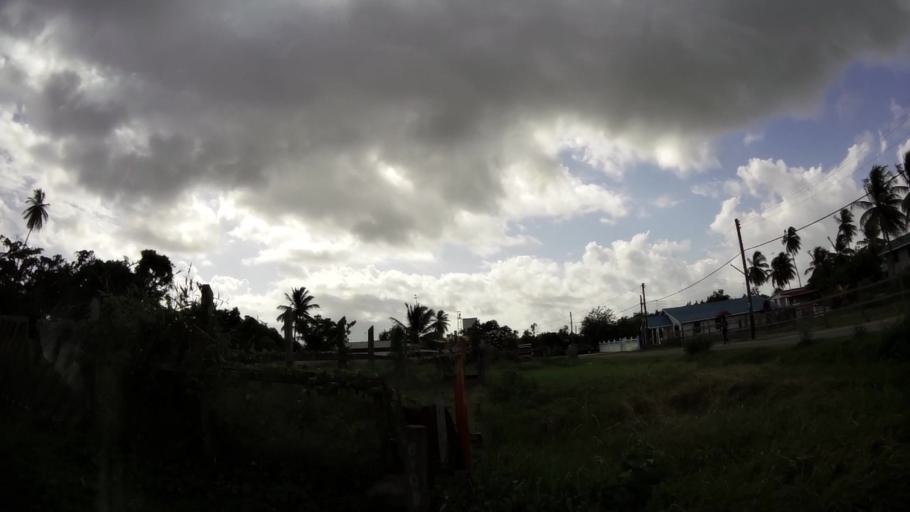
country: GY
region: Demerara-Mahaica
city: Mahaica Village
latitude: 6.6694
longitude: -57.9264
